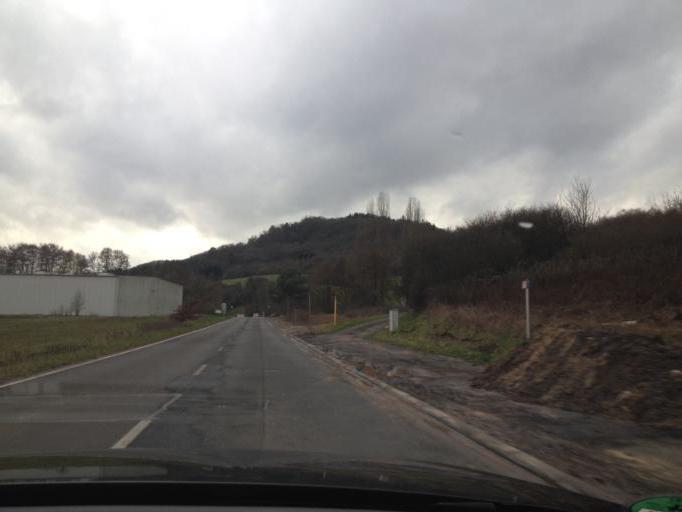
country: DE
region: Rheinland-Pfalz
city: Hintertiefenbach
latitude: 49.7205
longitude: 7.3723
